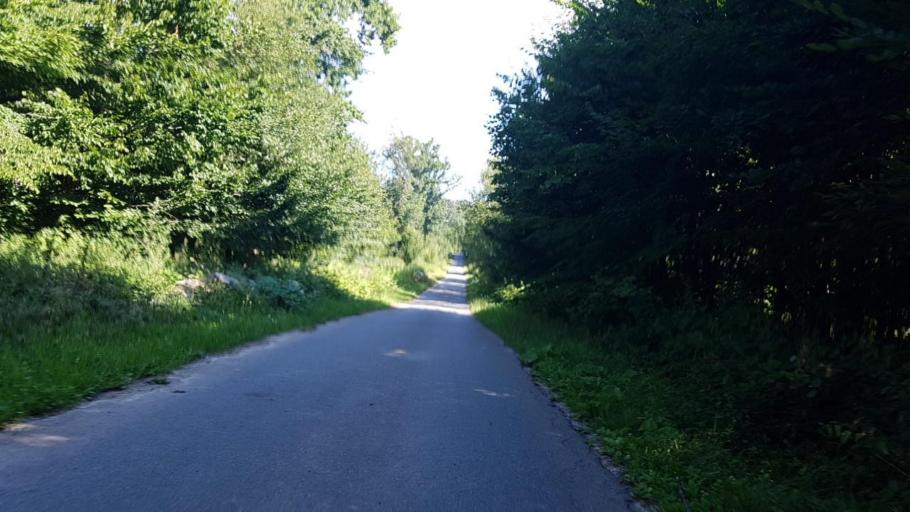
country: FR
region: Picardie
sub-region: Departement de l'Oise
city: Fleurines
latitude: 49.2597
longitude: 2.6196
